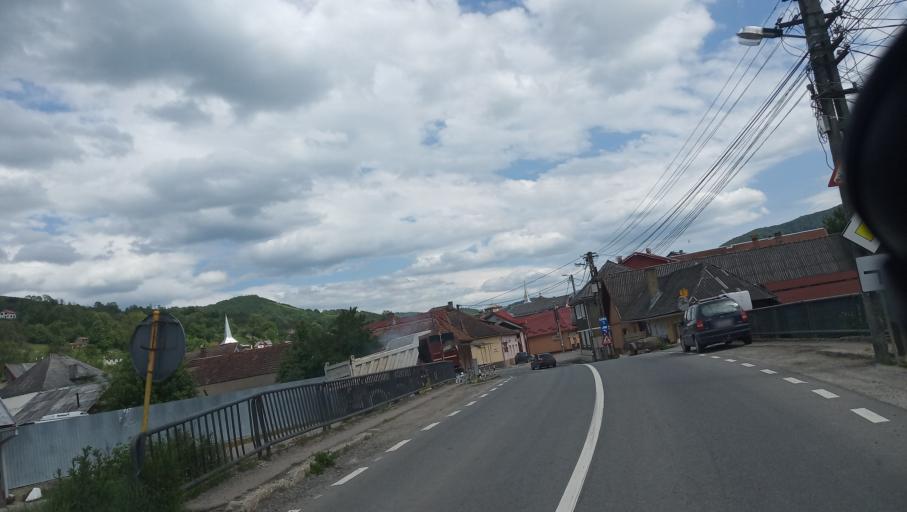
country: RO
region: Alba
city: Abrud
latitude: 46.2763
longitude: 23.0596
